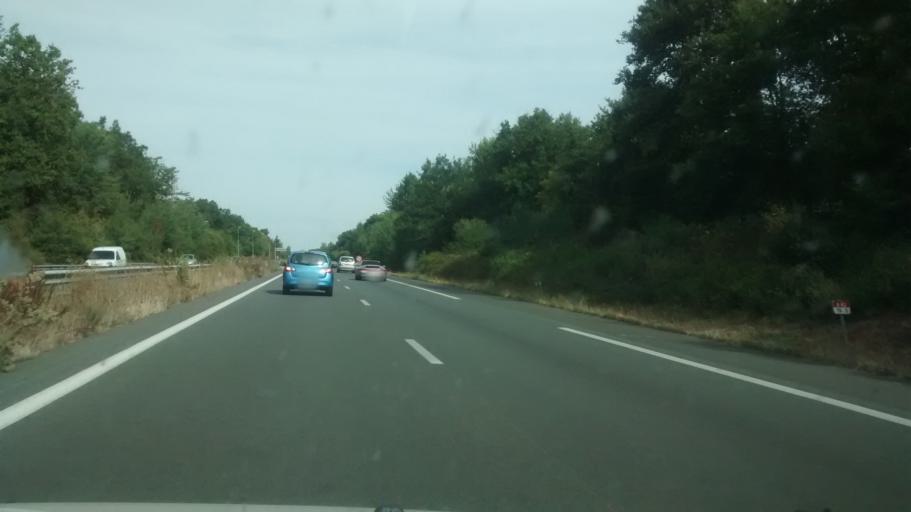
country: FR
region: Aquitaine
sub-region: Departement du Lot-et-Garonne
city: Fourques-sur-Garonne
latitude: 44.4046
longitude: 0.1860
